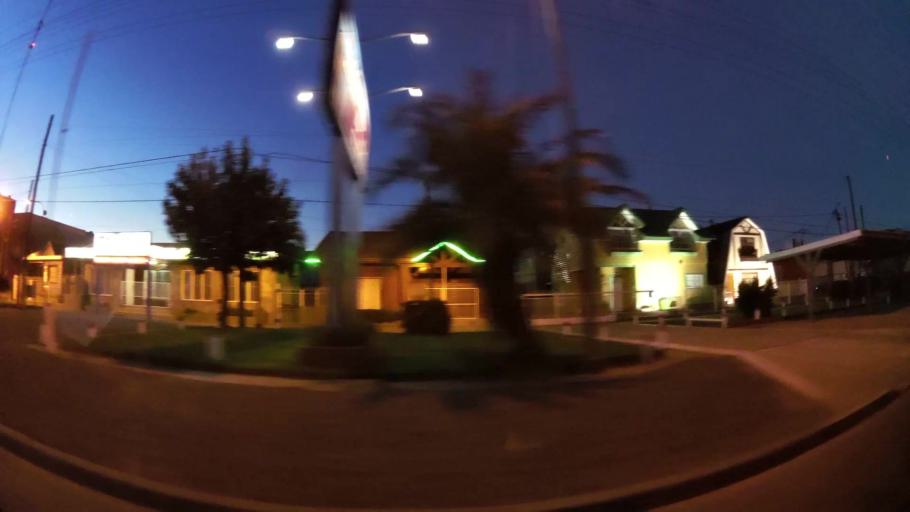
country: AR
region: Buenos Aires
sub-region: Partido de Almirante Brown
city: Adrogue
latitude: -34.7492
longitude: -58.3365
